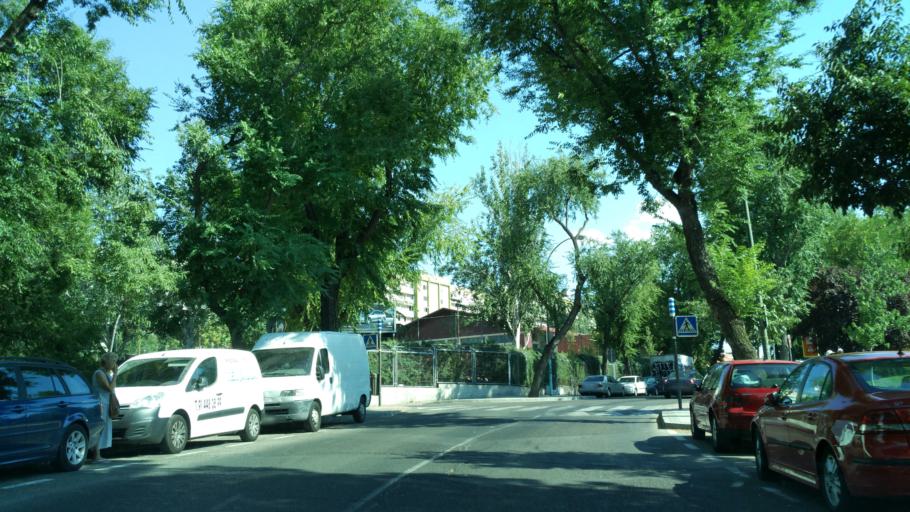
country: ES
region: Madrid
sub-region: Provincia de Madrid
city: Tetuan de las Victorias
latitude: 40.4623
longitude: -3.7125
